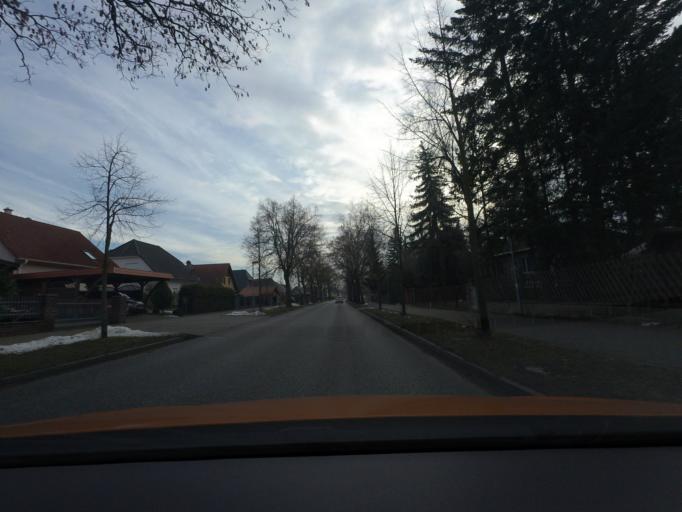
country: DE
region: Berlin
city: Blankenfelde
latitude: 52.6422
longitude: 13.3764
